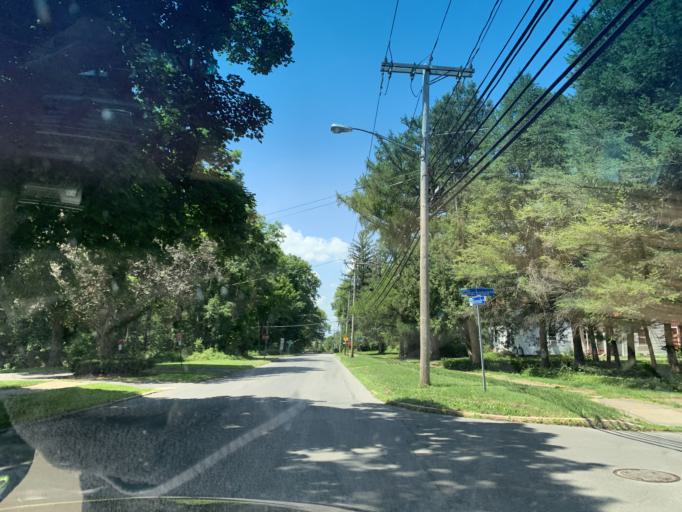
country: US
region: New York
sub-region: Oneida County
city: Utica
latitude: 43.1211
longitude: -75.2230
